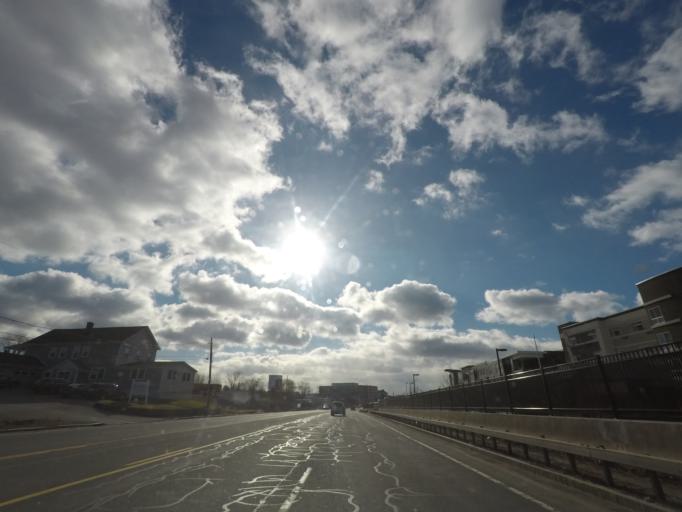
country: US
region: New York
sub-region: Schenectady County
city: Schenectady
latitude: 42.8267
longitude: -73.9305
